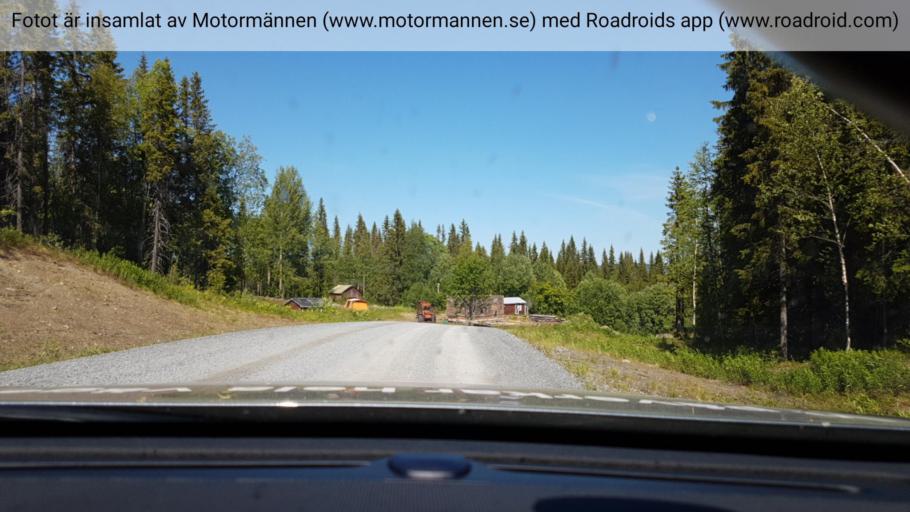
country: SE
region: Vaesterbotten
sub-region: Vilhelmina Kommun
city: Sjoberg
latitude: 64.7881
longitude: 15.9767
